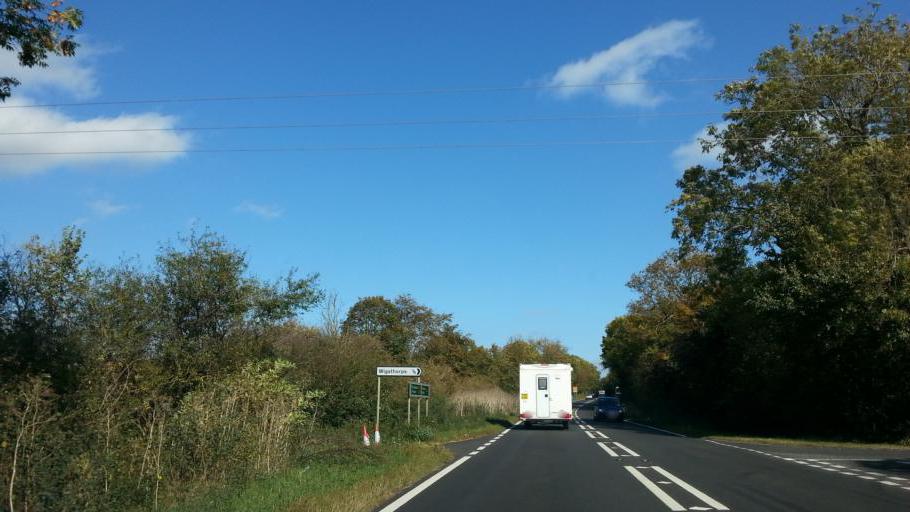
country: GB
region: England
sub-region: Northamptonshire
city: Oundle
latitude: 52.4375
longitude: -0.4759
